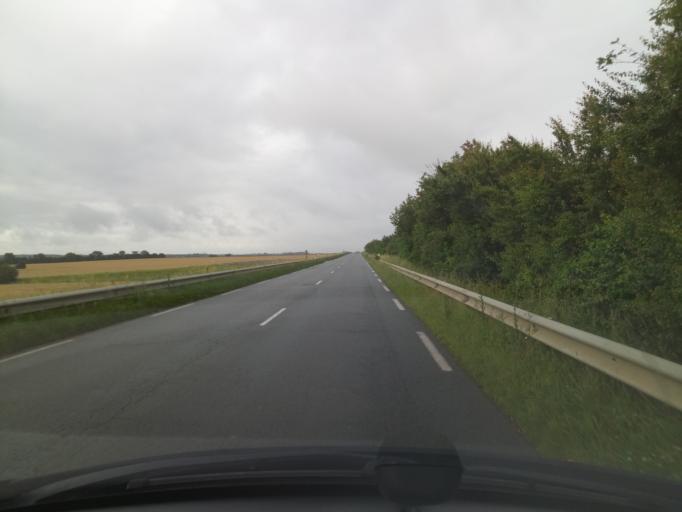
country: FR
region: Poitou-Charentes
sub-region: Departement de la Charente-Maritime
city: Saint-Jean-de-Liversay
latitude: 46.2066
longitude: -0.8741
